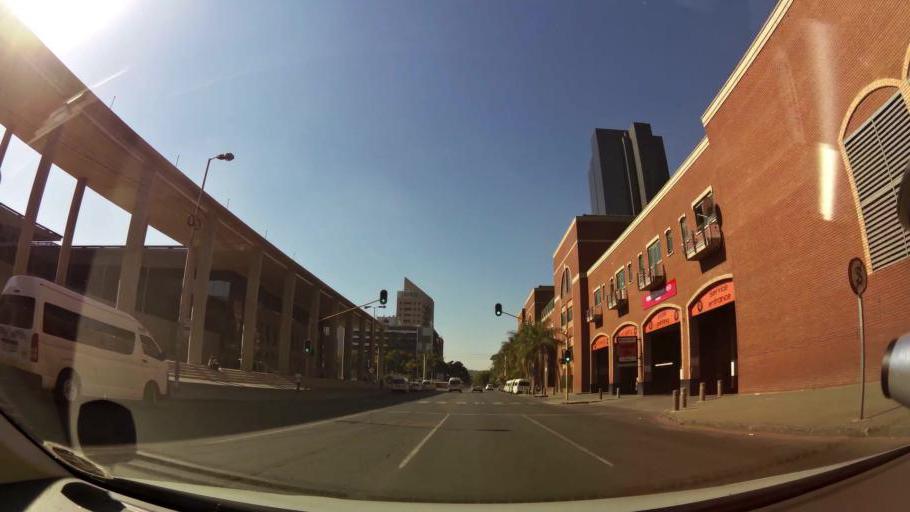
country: ZA
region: Gauteng
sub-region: City of Tshwane Metropolitan Municipality
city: Pretoria
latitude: -25.7445
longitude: 28.1936
